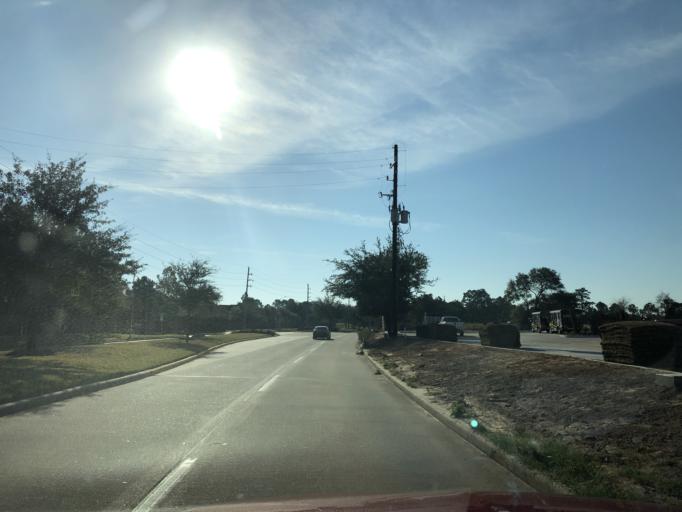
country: US
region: Texas
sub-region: Harris County
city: Tomball
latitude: 30.0478
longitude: -95.5641
